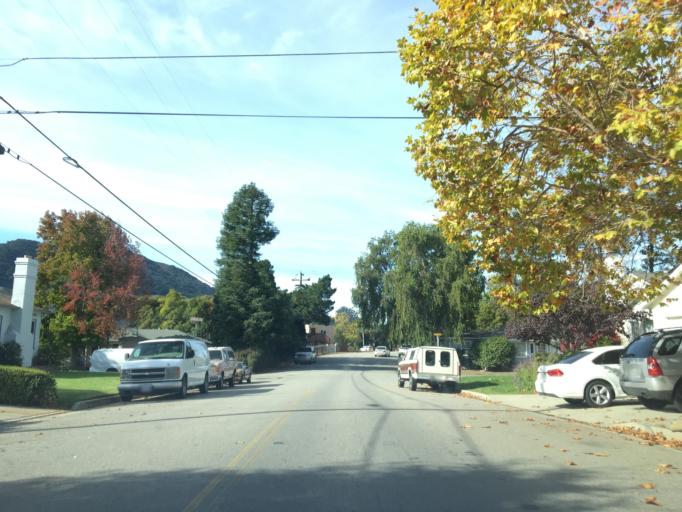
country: US
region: California
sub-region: San Luis Obispo County
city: San Luis Obispo
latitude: 35.2890
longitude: -120.6617
